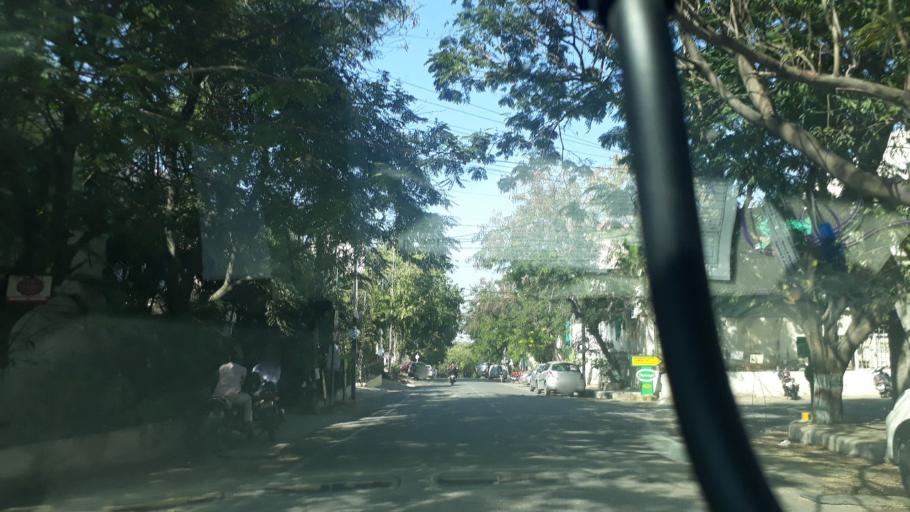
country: IN
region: Telangana
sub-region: Rangareddi
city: Kukatpalli
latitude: 17.4198
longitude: 78.4000
